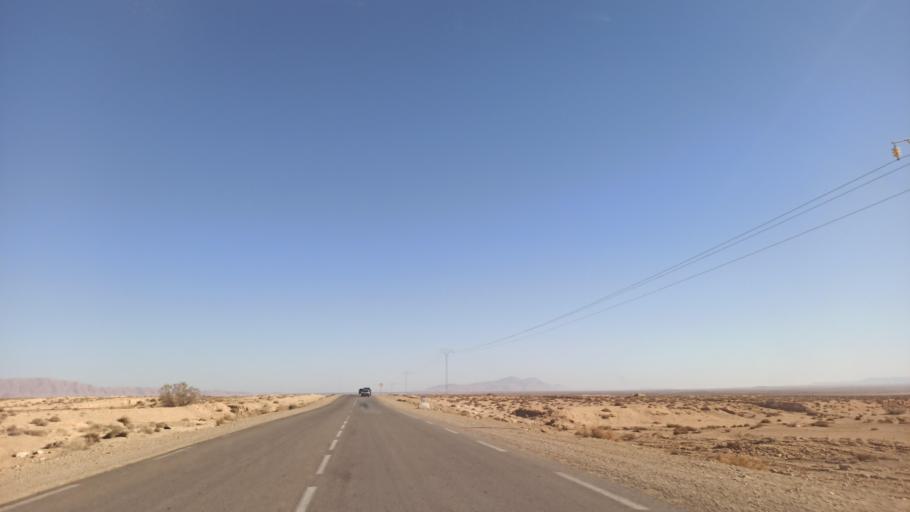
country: TN
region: Gafsa
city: Al Metlaoui
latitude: 34.3259
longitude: 8.5391
